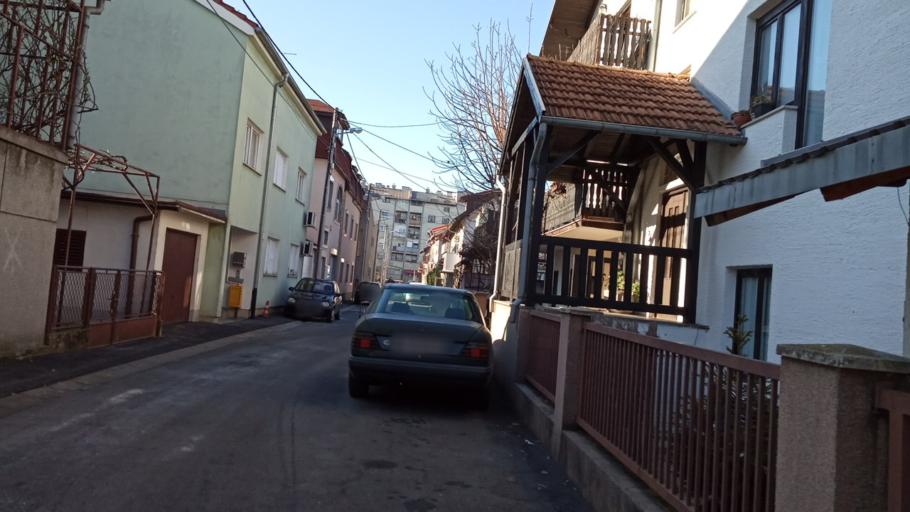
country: HR
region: Grad Zagreb
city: Jankomir
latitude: 45.7905
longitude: 15.9339
